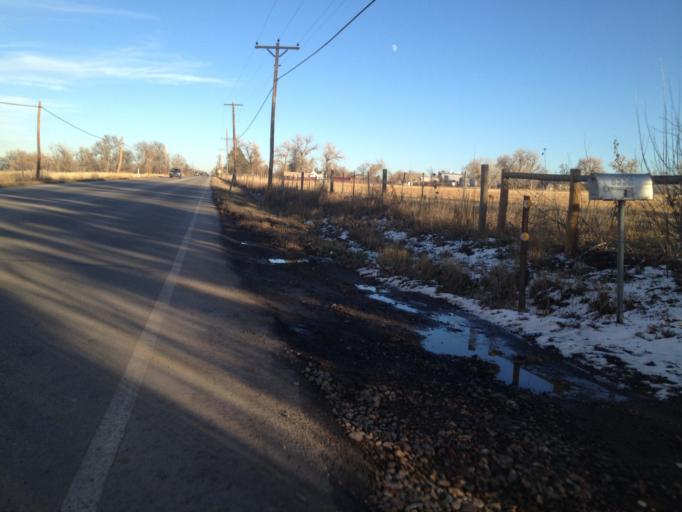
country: US
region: Colorado
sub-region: Boulder County
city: Louisville
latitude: 40.0146
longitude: -105.1585
